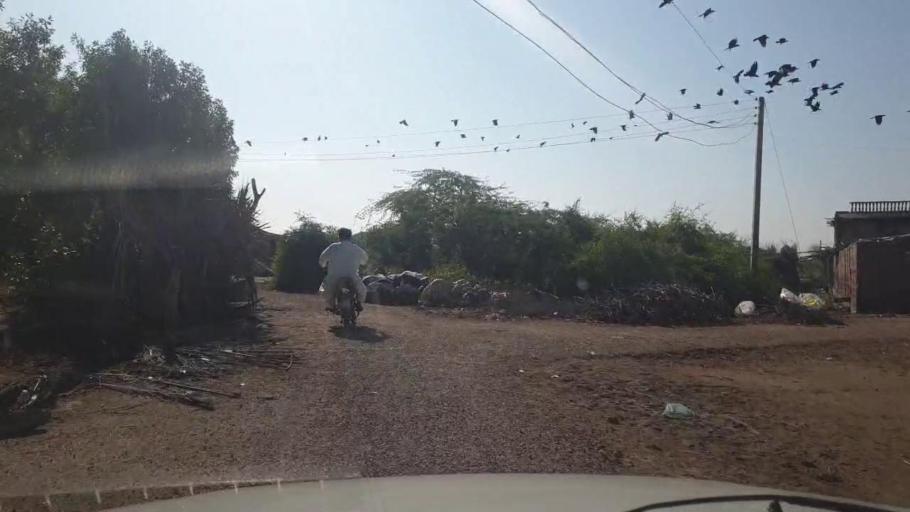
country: PK
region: Sindh
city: Chuhar Jamali
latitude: 24.4613
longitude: 67.9151
